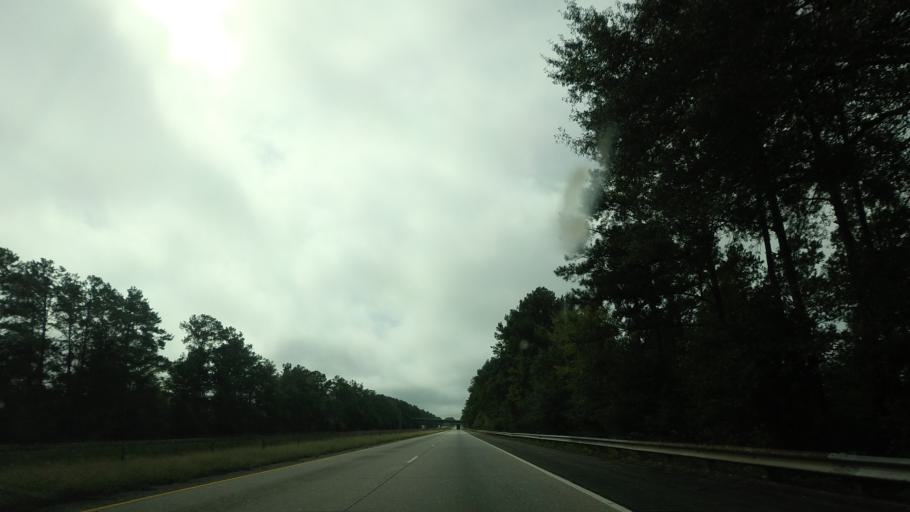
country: US
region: Georgia
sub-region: Bibb County
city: Macon
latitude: 32.7770
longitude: -83.5584
